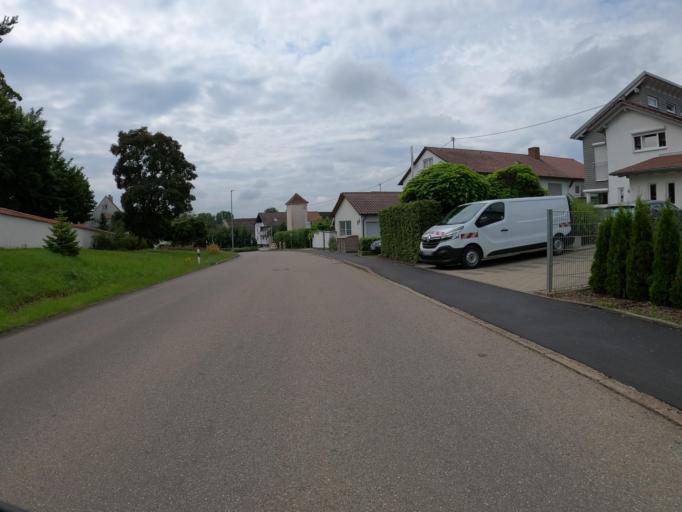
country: DE
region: Baden-Wuerttemberg
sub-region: Tuebingen Region
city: Langenau
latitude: 48.5057
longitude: 10.1339
